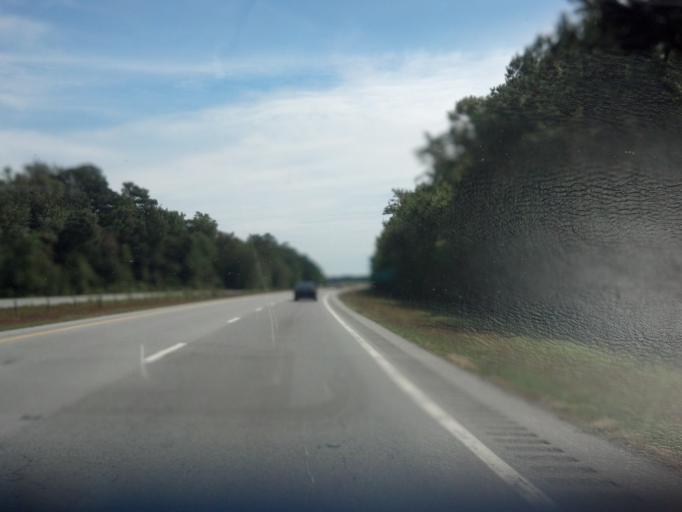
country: US
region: North Carolina
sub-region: Pitt County
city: Farmville
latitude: 35.6107
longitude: -77.4976
